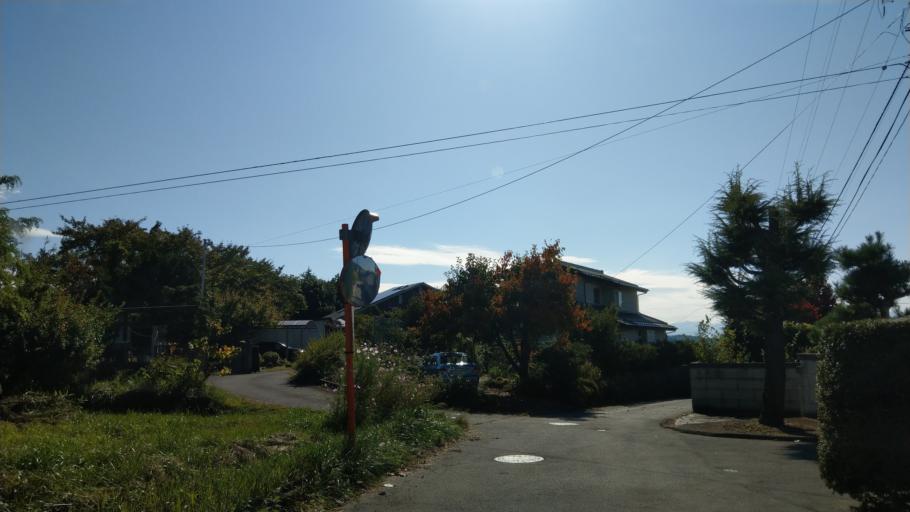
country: JP
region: Nagano
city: Komoro
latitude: 36.3356
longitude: 138.4351
